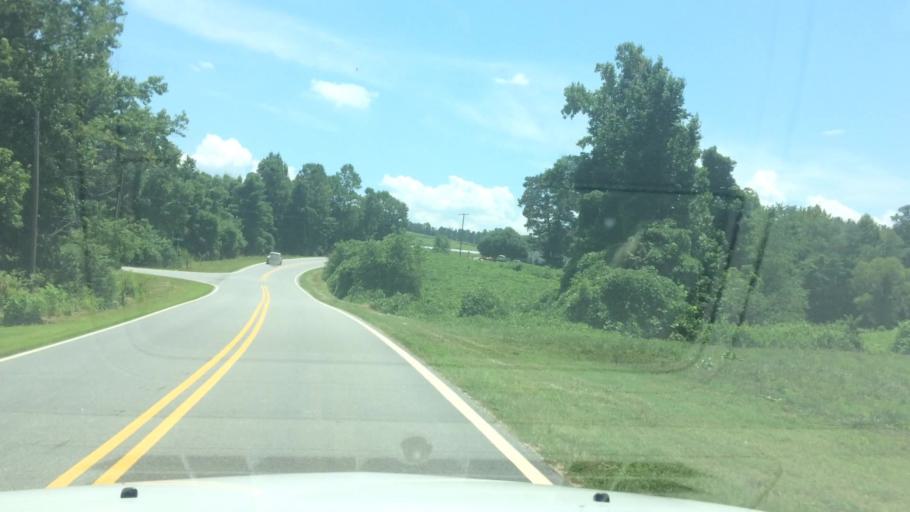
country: US
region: North Carolina
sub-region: Alexander County
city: Taylorsville
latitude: 35.9324
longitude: -81.2648
